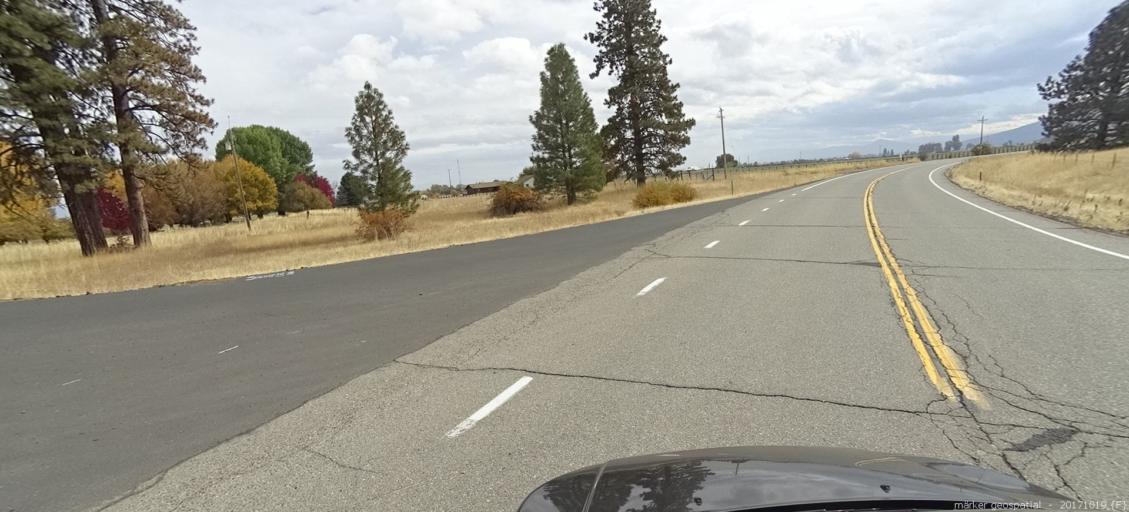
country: US
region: California
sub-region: Shasta County
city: Burney
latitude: 41.0933
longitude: -121.5150
